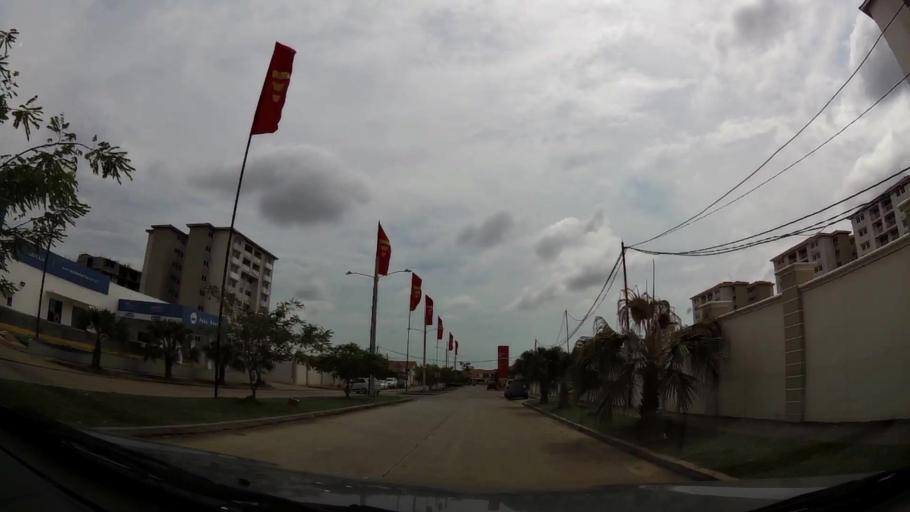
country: PA
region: Panama
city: San Miguelito
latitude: 9.0423
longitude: -79.4170
